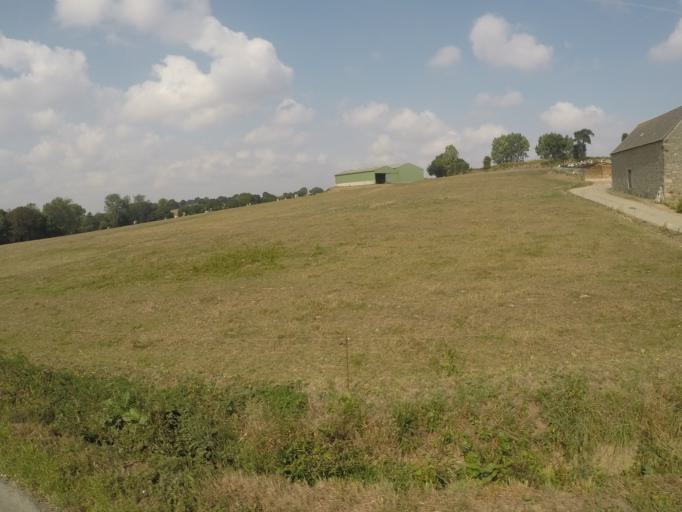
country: FR
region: Brittany
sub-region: Departement des Cotes-d'Armor
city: Saint-Donan
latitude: 48.5143
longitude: -2.9050
